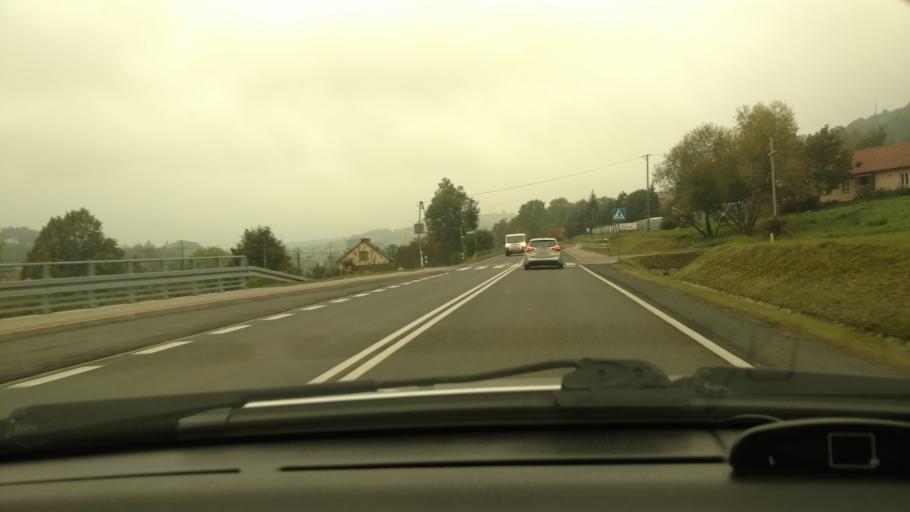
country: PL
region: Lesser Poland Voivodeship
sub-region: Powiat nowosadecki
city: Grybow
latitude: 49.6237
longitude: 20.9257
